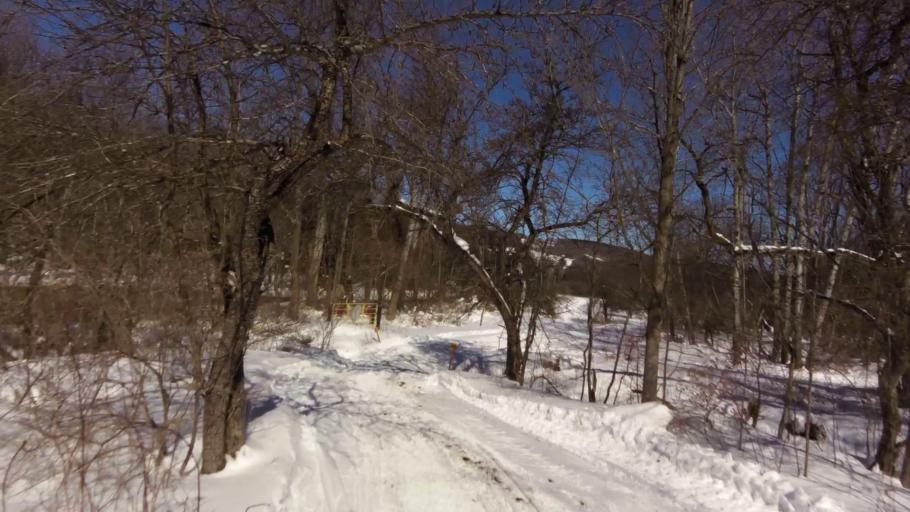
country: US
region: New York
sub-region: Allegany County
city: Cuba
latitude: 42.3314
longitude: -78.2498
